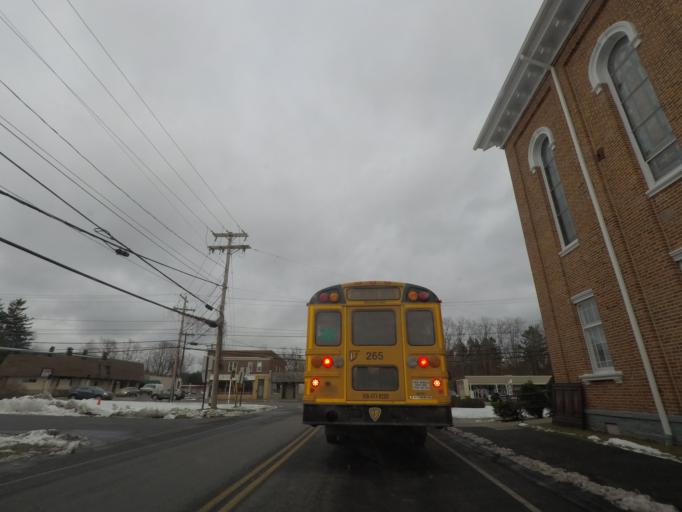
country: US
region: New York
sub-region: Rensselaer County
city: East Greenbush
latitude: 42.5885
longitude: -73.7000
